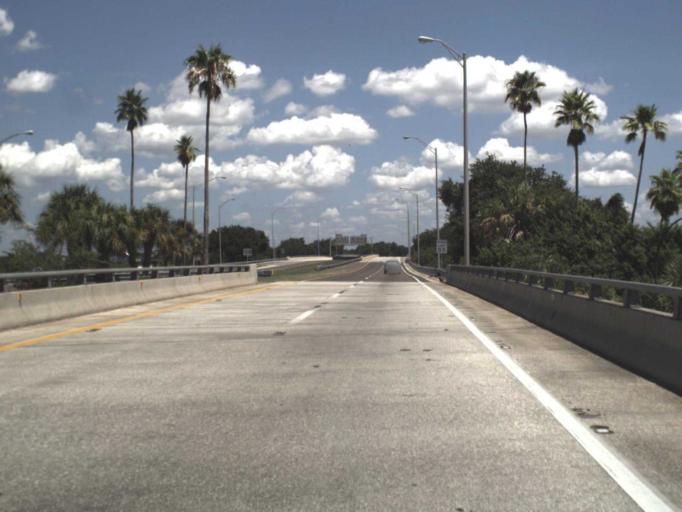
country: US
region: Florida
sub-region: Hillsborough County
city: Tampa
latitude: 27.8936
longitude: -82.5078
